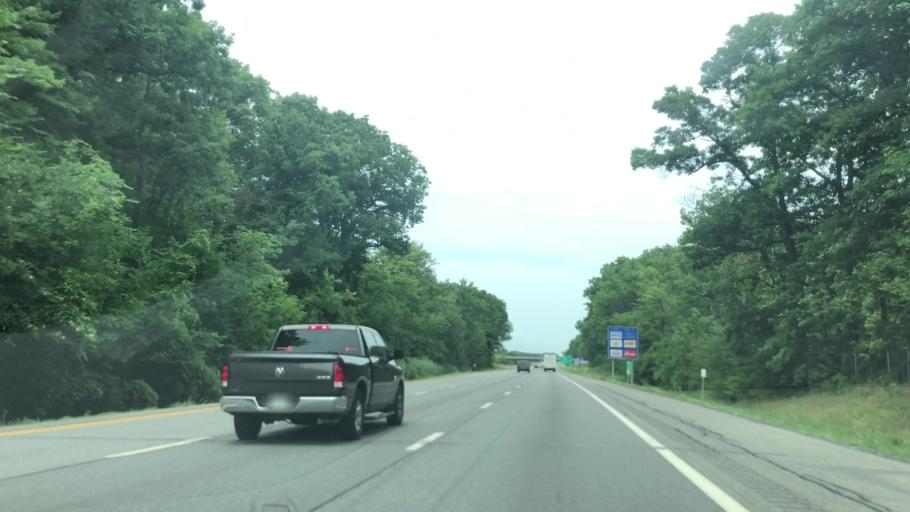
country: US
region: New York
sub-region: Saratoga County
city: Country Knolls
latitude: 42.8482
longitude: -73.7724
